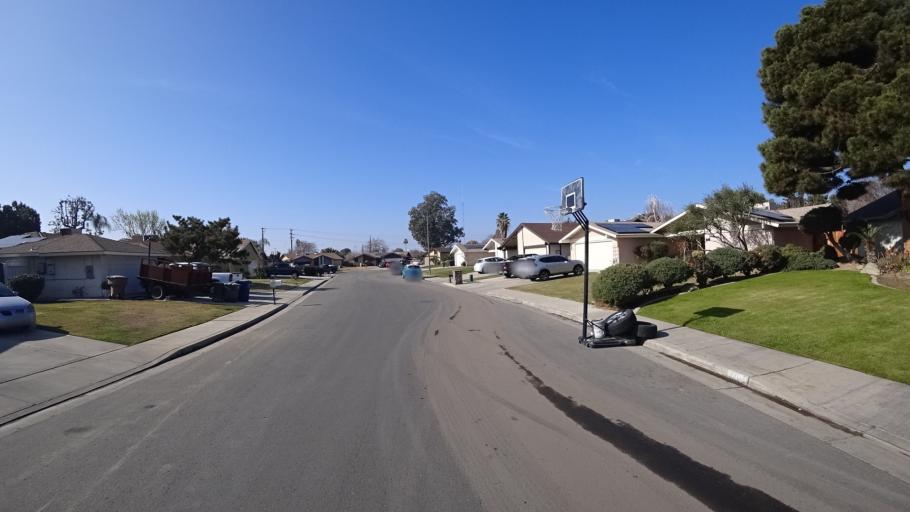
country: US
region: California
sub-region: Kern County
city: Bakersfield
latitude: 35.3297
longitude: -119.0552
